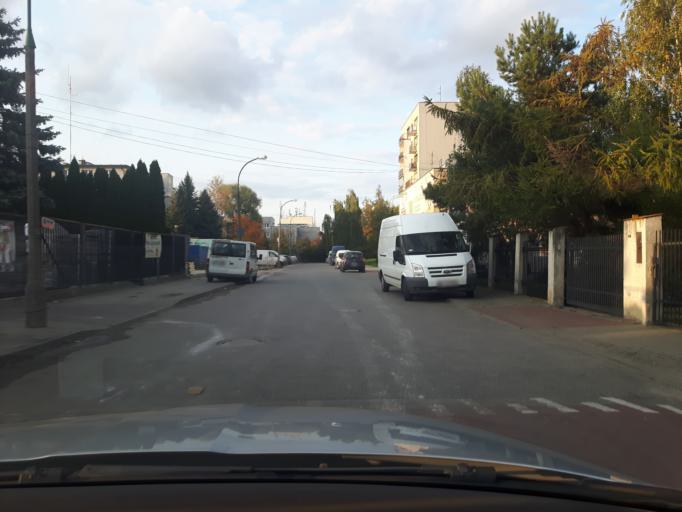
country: PL
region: Masovian Voivodeship
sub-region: Warszawa
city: Ursynow
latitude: 52.1532
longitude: 21.0199
